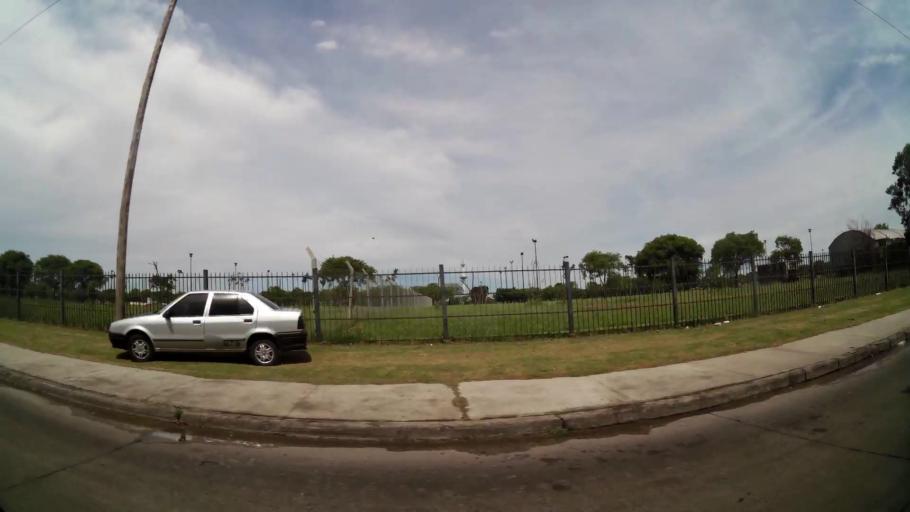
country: AR
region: Buenos Aires F.D.
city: Villa Lugano
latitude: -34.6612
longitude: -58.4654
